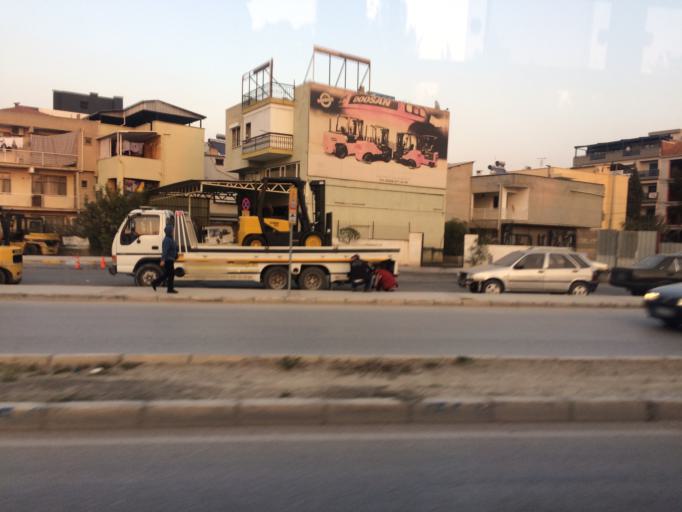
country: TR
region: Izmir
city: Karsiyaka
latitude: 38.4977
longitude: 27.0486
